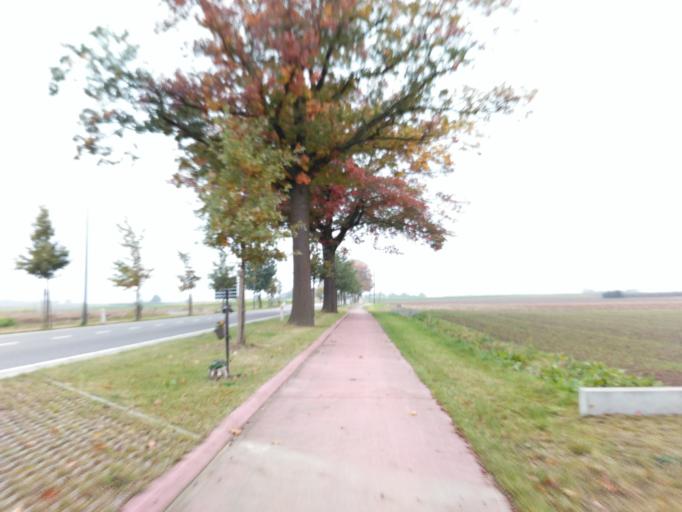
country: BE
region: Flanders
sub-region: Provincie Limburg
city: Riemst
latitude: 50.8612
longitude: 5.5990
